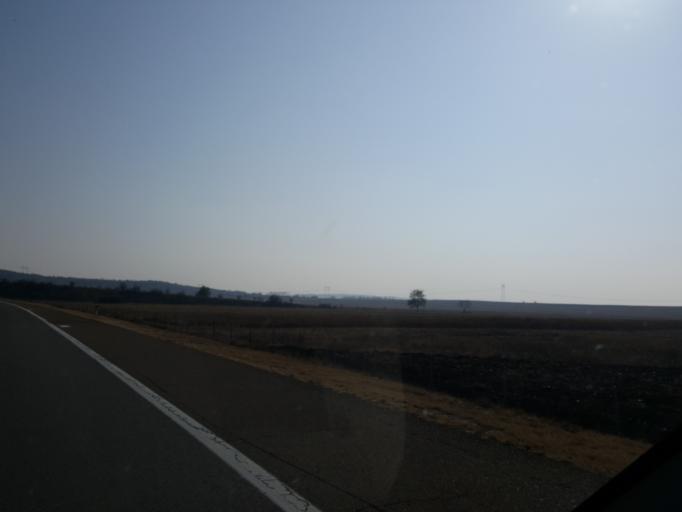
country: RS
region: Central Serbia
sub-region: Nisavski Okrug
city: Doljevac
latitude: 43.2370
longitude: 21.8199
